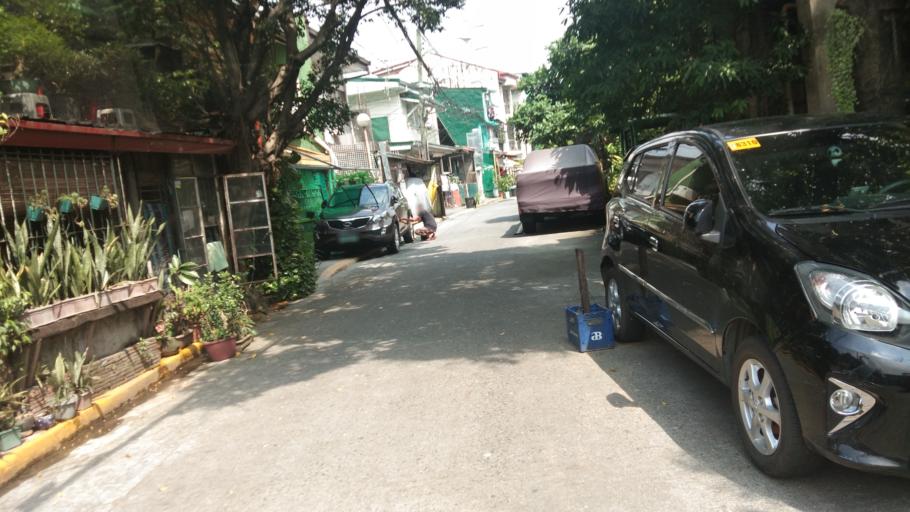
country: PH
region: Metro Manila
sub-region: City of Manila
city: Quiapo
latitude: 14.5764
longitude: 120.9985
